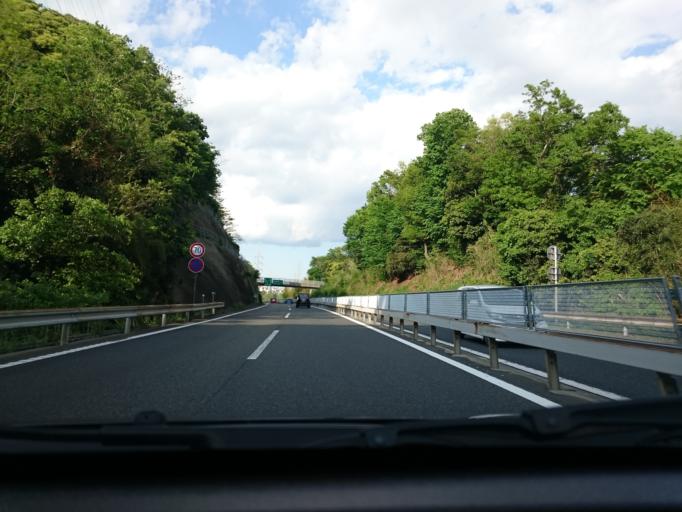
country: JP
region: Kanagawa
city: Oiso
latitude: 35.3292
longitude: 139.2897
